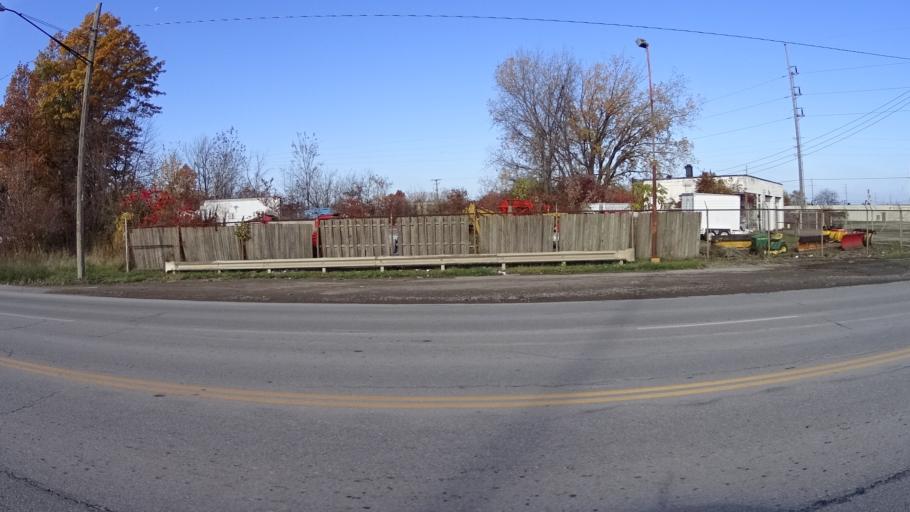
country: US
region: Ohio
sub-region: Lorain County
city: Lorain
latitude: 41.4619
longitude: -82.1584
